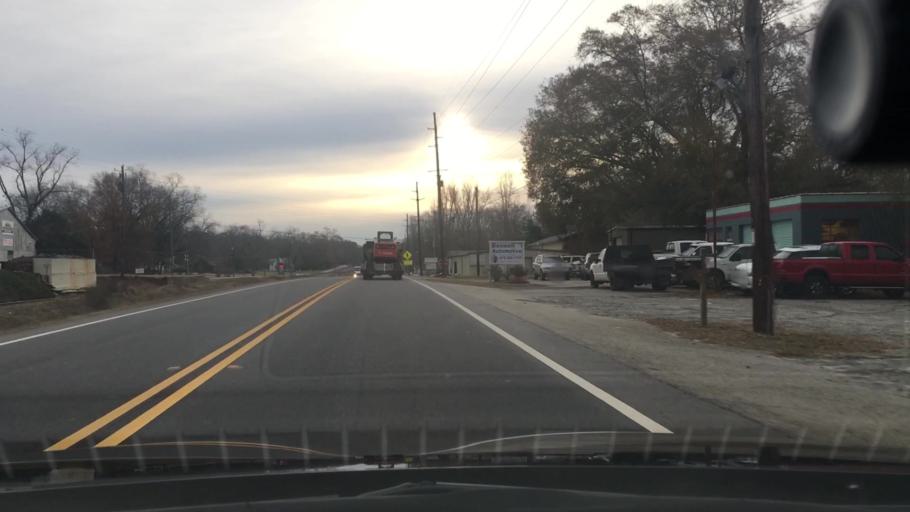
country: US
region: Georgia
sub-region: Fayette County
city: Peachtree City
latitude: 33.3269
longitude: -84.6373
